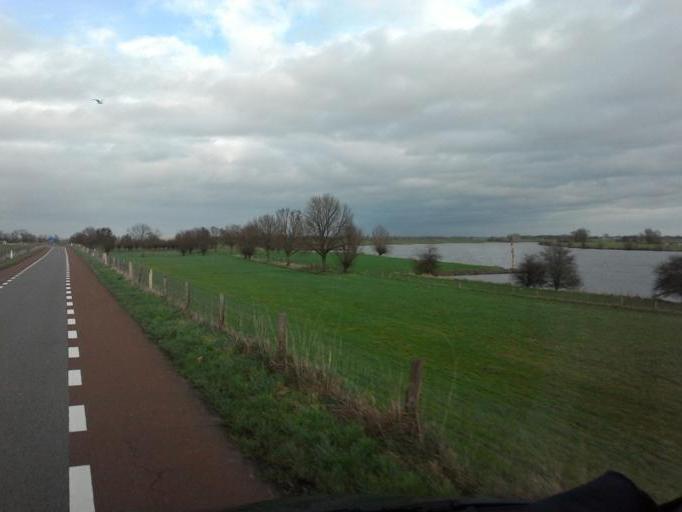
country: NL
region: Gelderland
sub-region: Gemeente Culemborg
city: Culemborg
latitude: 51.9751
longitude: 5.2267
